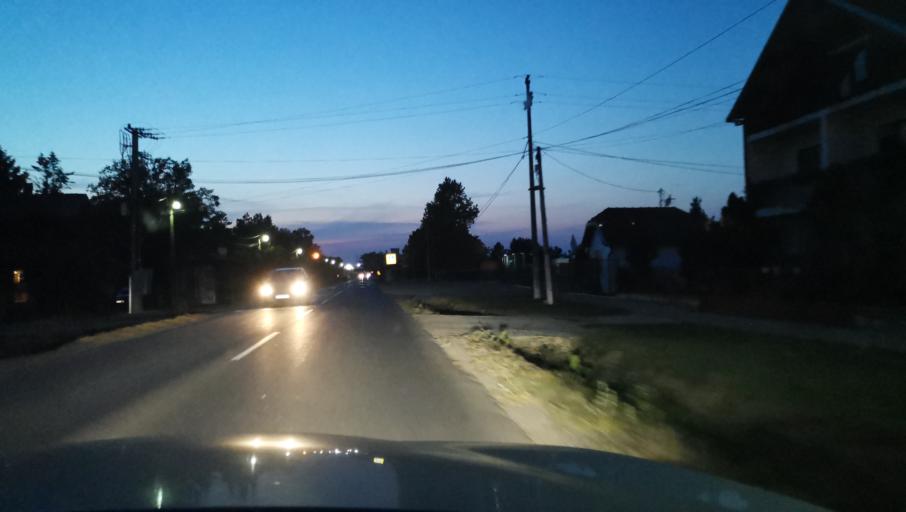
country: RS
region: Central Serbia
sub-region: Belgrade
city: Surcin
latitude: 44.7616
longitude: 20.2525
